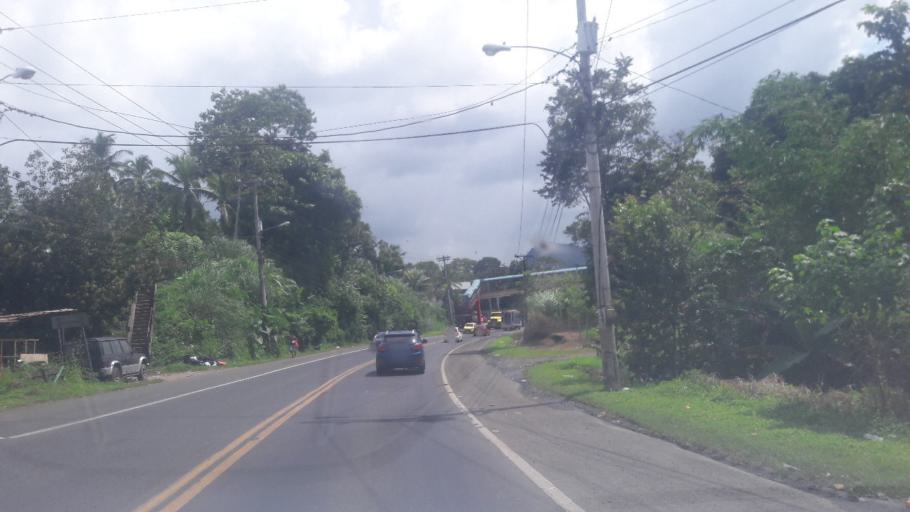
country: PA
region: Panama
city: Alcalde Diaz
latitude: 9.1260
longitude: -79.5773
